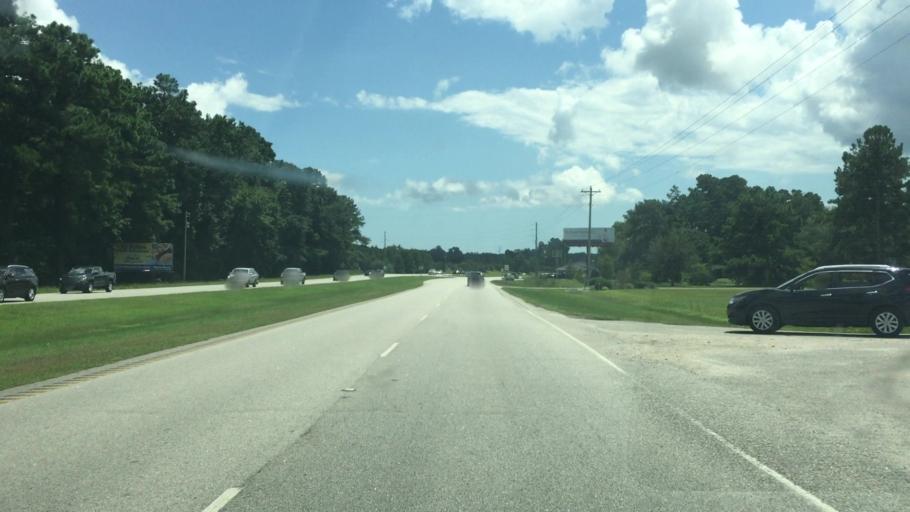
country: US
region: South Carolina
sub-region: Horry County
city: Little River
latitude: 33.9570
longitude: -78.7365
